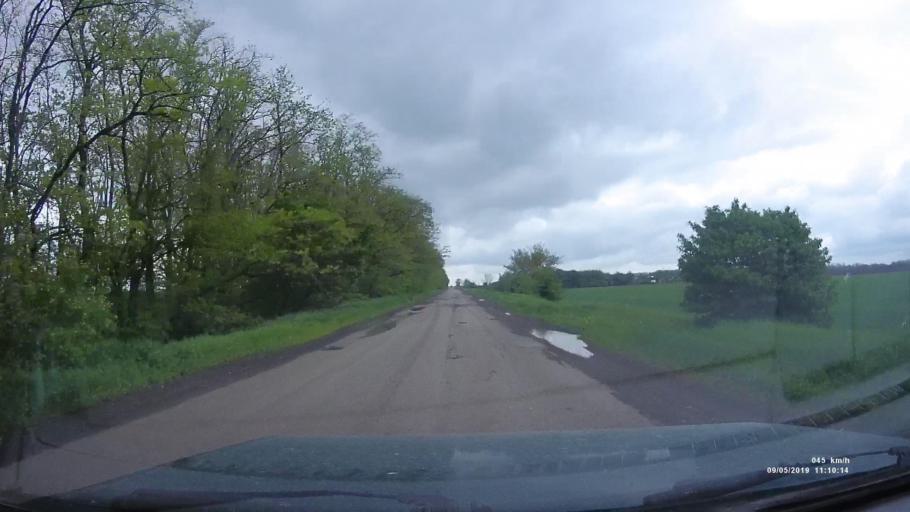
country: RU
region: Krasnodarskiy
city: Kanelovskaya
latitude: 46.7770
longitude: 39.2115
